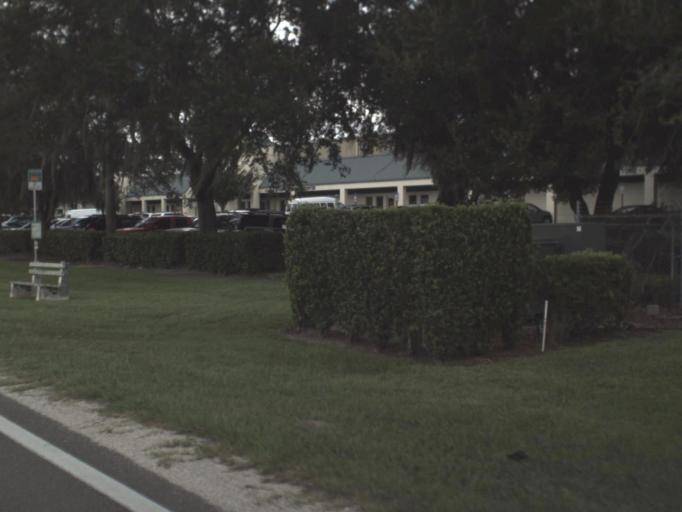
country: US
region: Florida
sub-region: Polk County
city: Winston
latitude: 27.9967
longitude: -82.0067
